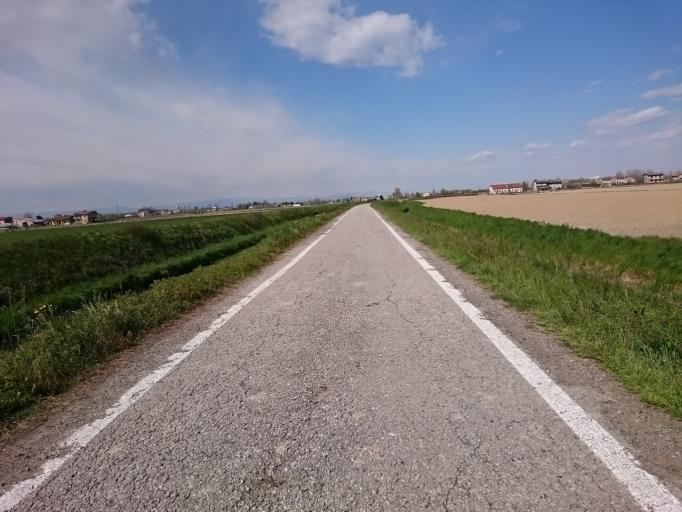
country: IT
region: Veneto
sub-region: Provincia di Padova
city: Legnaro
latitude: 45.3316
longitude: 11.9455
